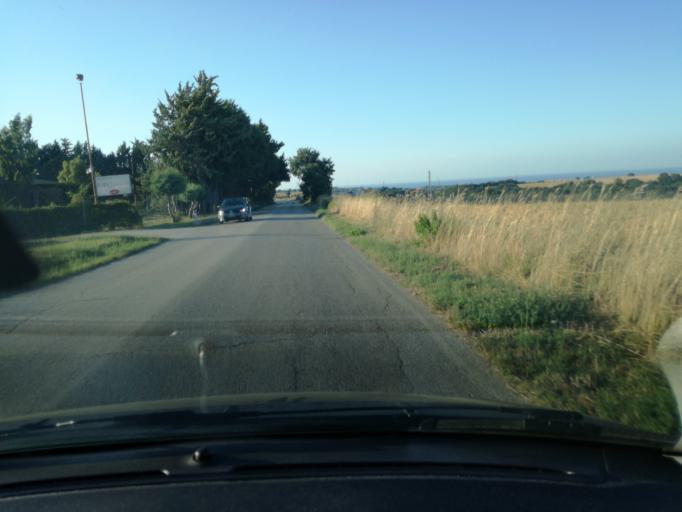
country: IT
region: Molise
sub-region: Provincia di Campobasso
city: San Giacomo degli Schiavoni
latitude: 41.9463
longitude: 14.9425
